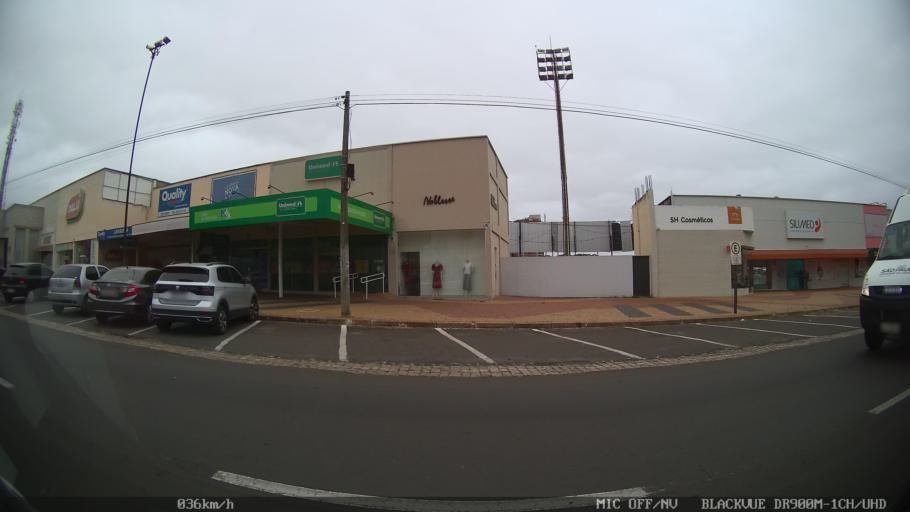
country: BR
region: Sao Paulo
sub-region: Sao Jose Do Rio Preto
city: Sao Jose do Rio Preto
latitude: -20.8350
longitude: -49.4003
